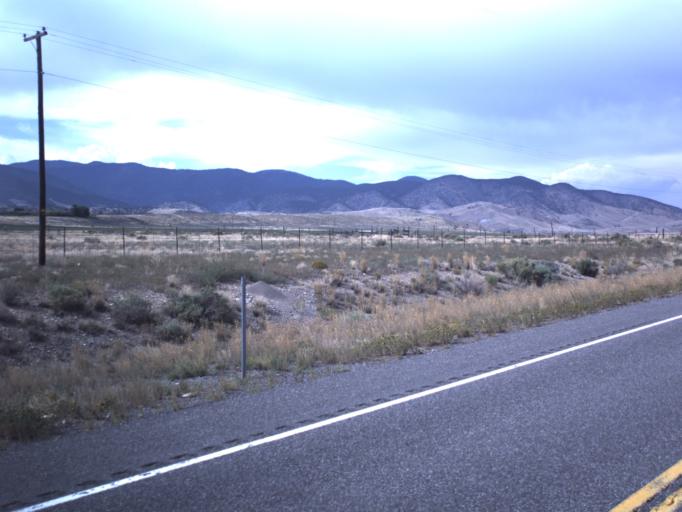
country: US
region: Utah
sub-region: Piute County
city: Junction
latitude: 38.4155
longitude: -112.2314
